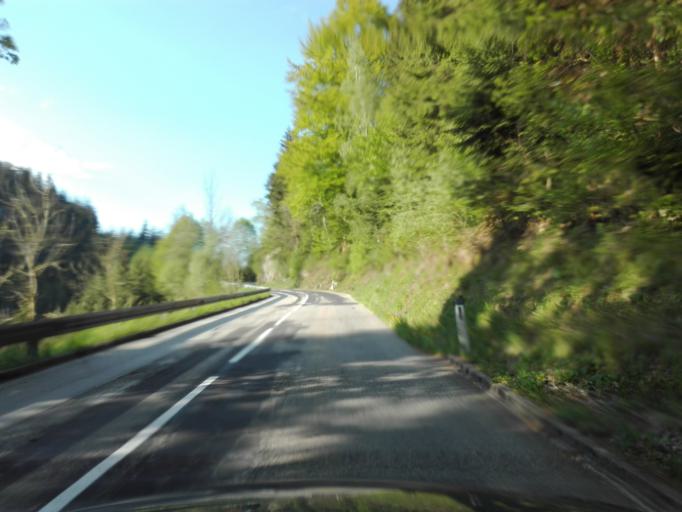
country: AT
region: Upper Austria
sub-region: Politischer Bezirk Rohrbach
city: Atzesberg
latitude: 48.4787
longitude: 13.9314
